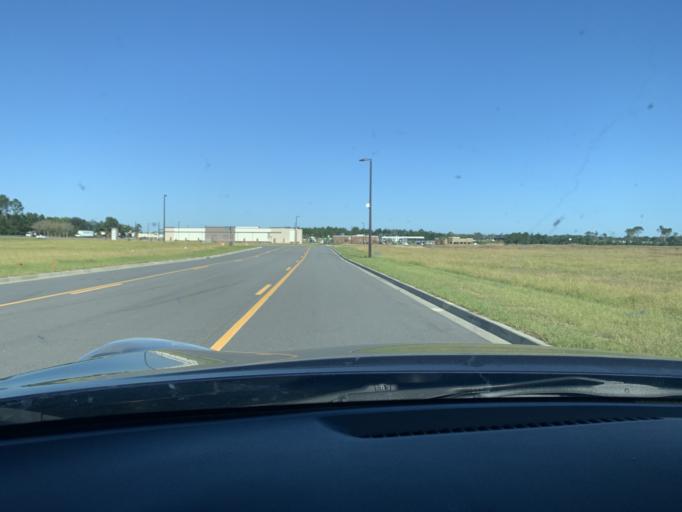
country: US
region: Georgia
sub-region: Chatham County
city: Pooler
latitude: 32.0762
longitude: -81.2787
